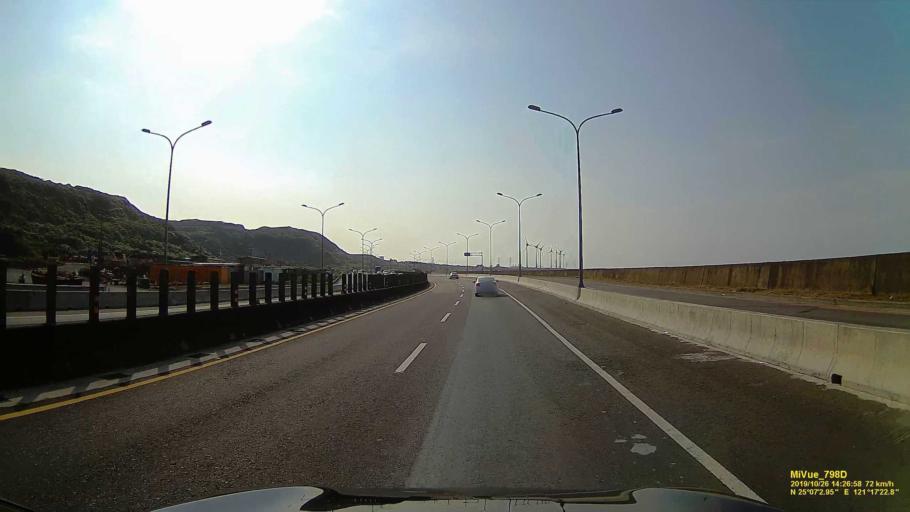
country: TW
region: Taiwan
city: Taoyuan City
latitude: 25.1174
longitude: 121.2894
